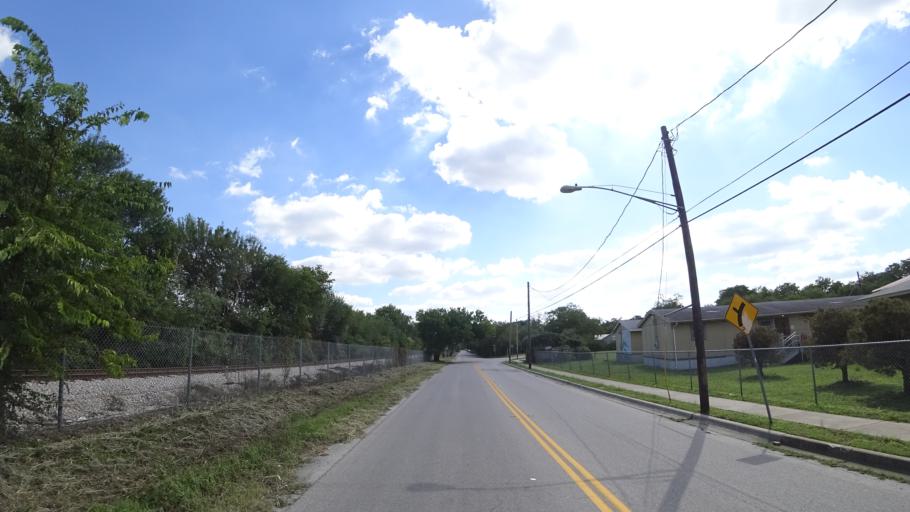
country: US
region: Texas
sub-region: Travis County
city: Austin
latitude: 30.3112
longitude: -97.7158
